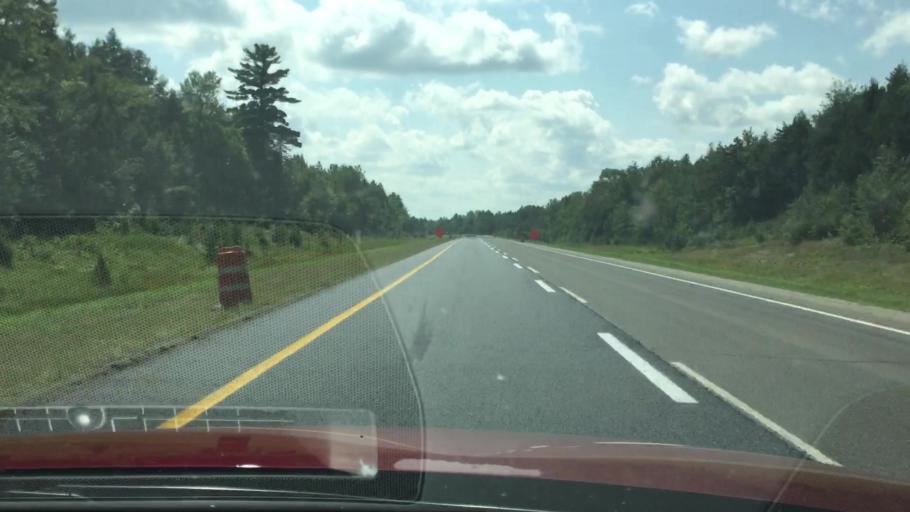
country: US
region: Maine
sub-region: Penobscot County
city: Medway
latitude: 45.7061
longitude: -68.4800
